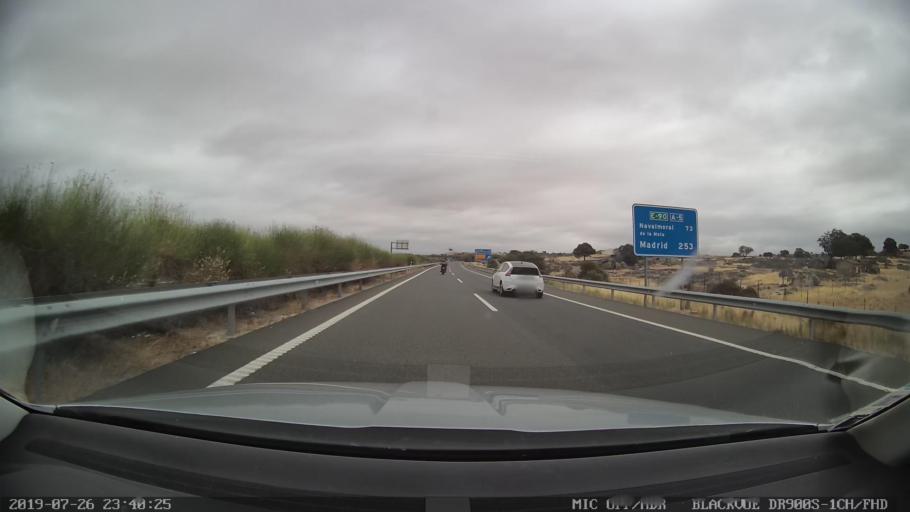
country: ES
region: Extremadura
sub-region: Provincia de Caceres
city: Trujillo
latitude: 39.4650
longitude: -5.8586
